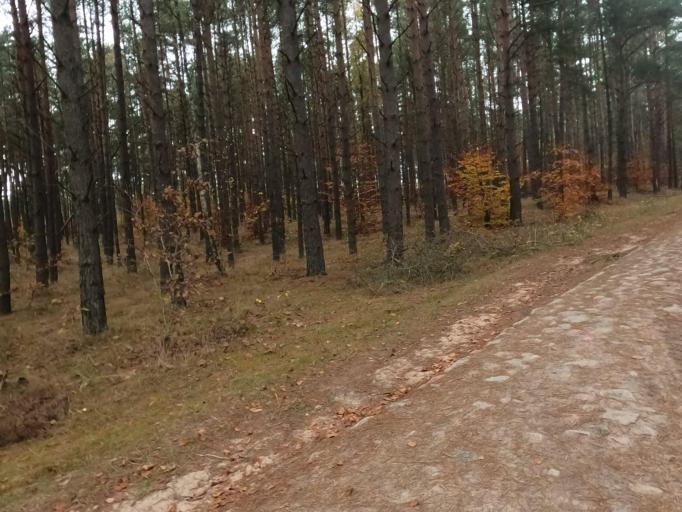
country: PL
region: Pomeranian Voivodeship
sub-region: Powiat starogardzki
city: Skarszewy
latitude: 54.0532
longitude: 18.4418
